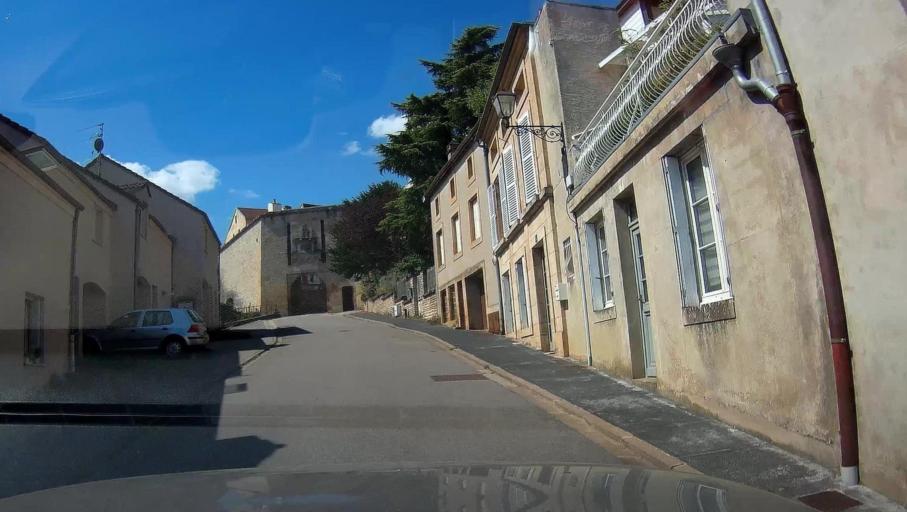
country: FR
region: Champagne-Ardenne
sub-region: Departement de la Haute-Marne
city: Langres
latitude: 47.8630
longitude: 5.3368
